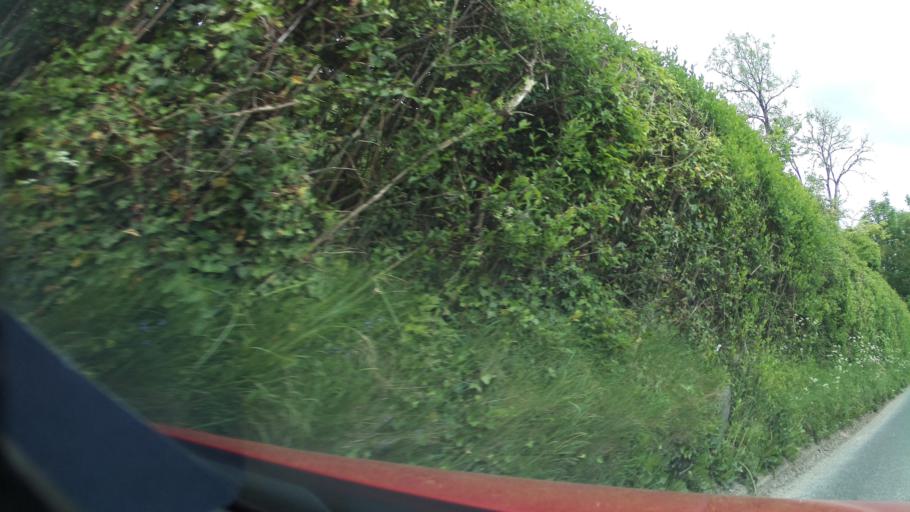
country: GB
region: England
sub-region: Dorset
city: Dorchester
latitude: 50.7477
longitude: -2.4641
